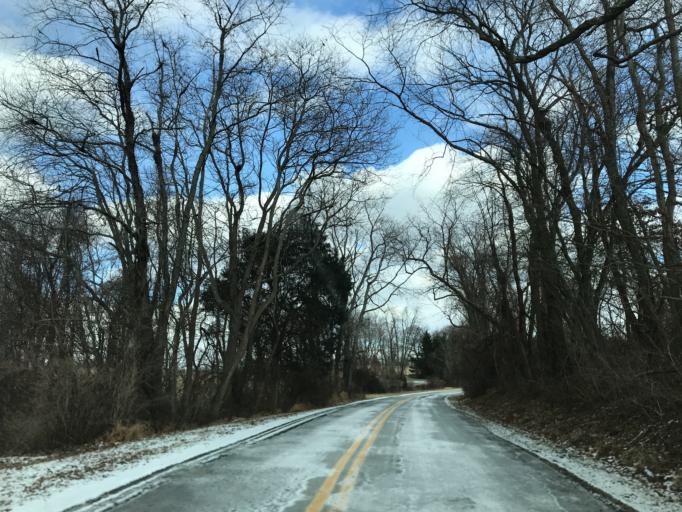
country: US
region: Maryland
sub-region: Harford County
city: Jarrettsville
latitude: 39.6381
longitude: -76.5140
